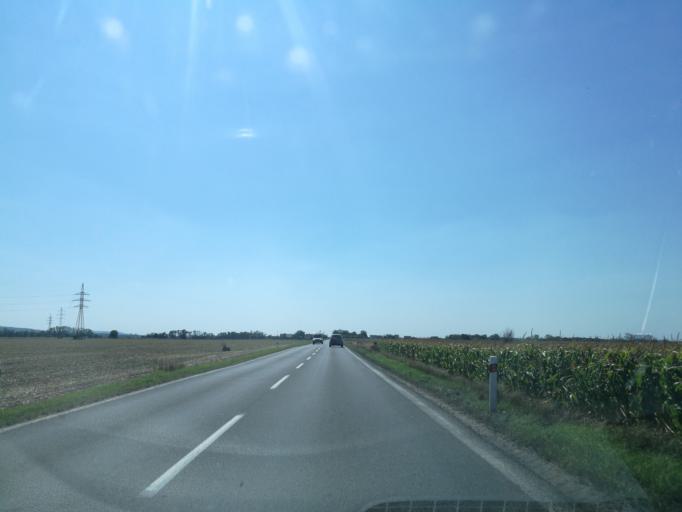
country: SK
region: Trnavsky
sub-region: Okres Trnava
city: Piestany
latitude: 48.5512
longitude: 17.8091
